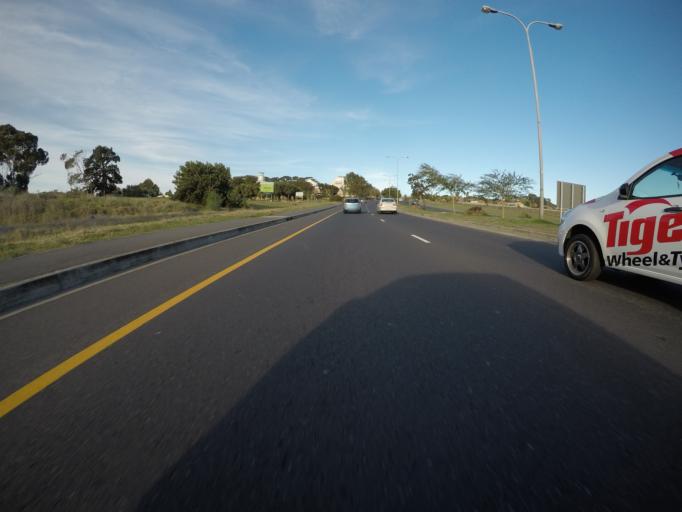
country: ZA
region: Western Cape
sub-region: City of Cape Town
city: Kraaifontein
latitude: -33.8576
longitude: 18.6684
